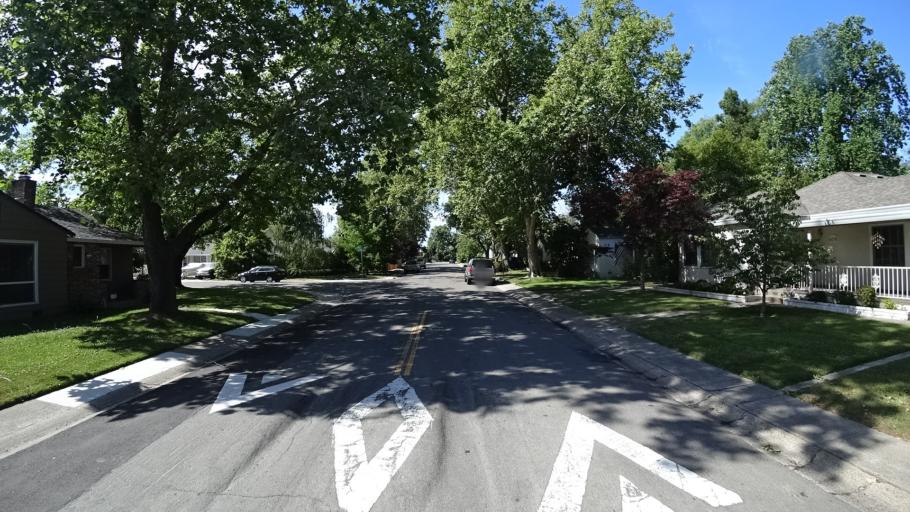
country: US
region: California
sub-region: Sacramento County
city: Sacramento
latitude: 38.5351
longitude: -121.4959
